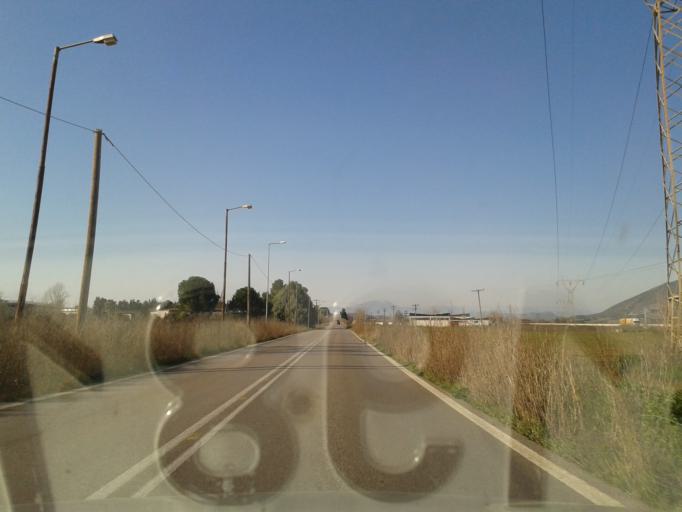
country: GR
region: Central Greece
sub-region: Nomos Voiotias
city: Arma
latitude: 38.3775
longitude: 23.4726
